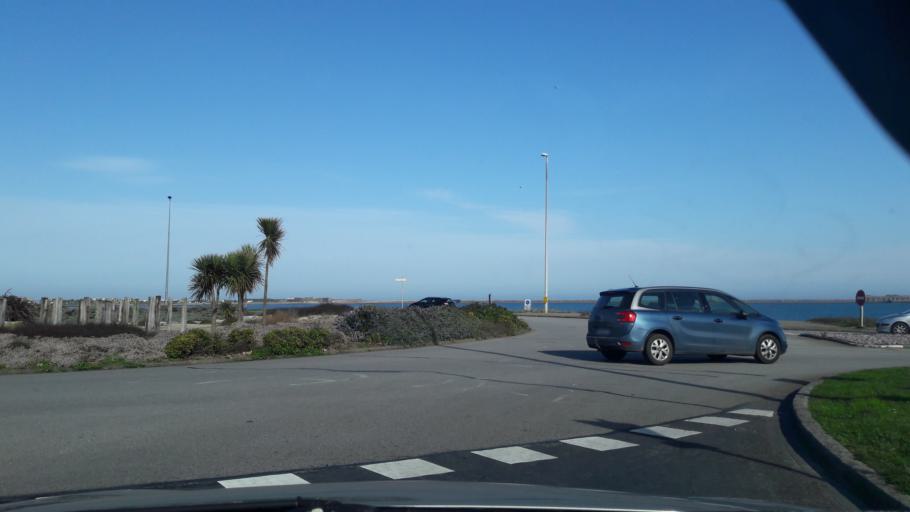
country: FR
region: Lower Normandy
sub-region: Departement de la Manche
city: Equeurdreville-Hainneville
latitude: 49.6573
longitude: -1.6677
